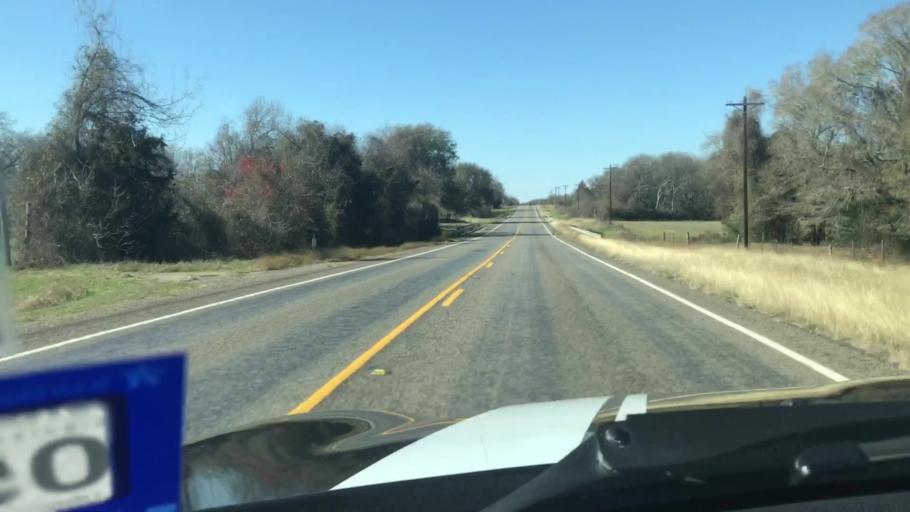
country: US
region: Texas
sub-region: Robertson County
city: Calvert
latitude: 30.8849
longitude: -96.7723
